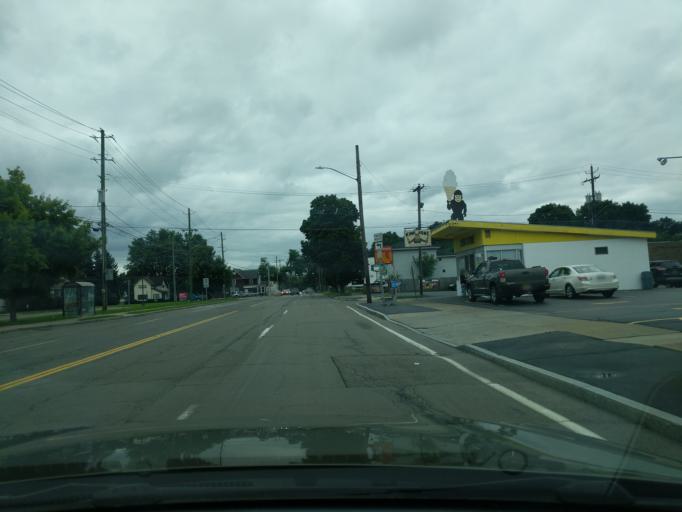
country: US
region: New York
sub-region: Chemung County
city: Elmira Heights
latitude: 42.1103
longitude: -76.8202
